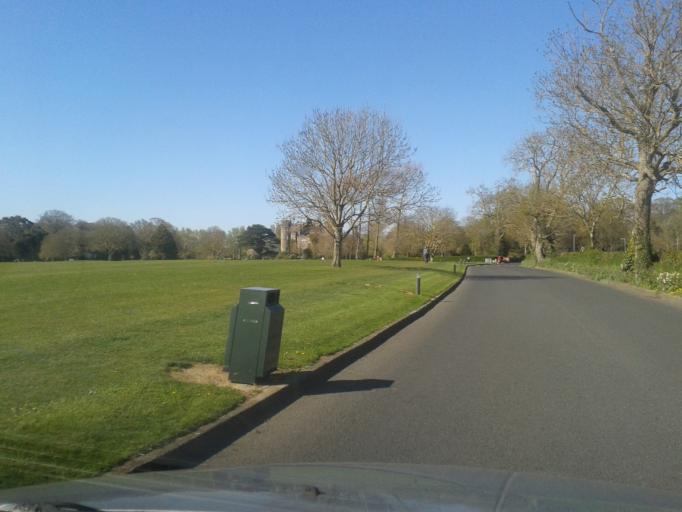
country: IE
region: Leinster
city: Malahide
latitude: 53.4420
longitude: -6.1638
